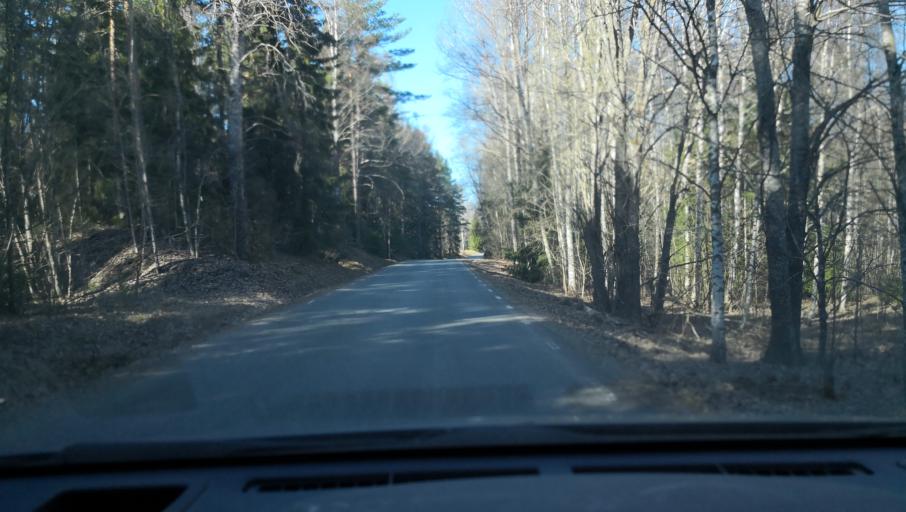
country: SE
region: Vaestmanland
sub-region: Sala Kommun
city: Sala
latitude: 59.9809
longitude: 16.4748
